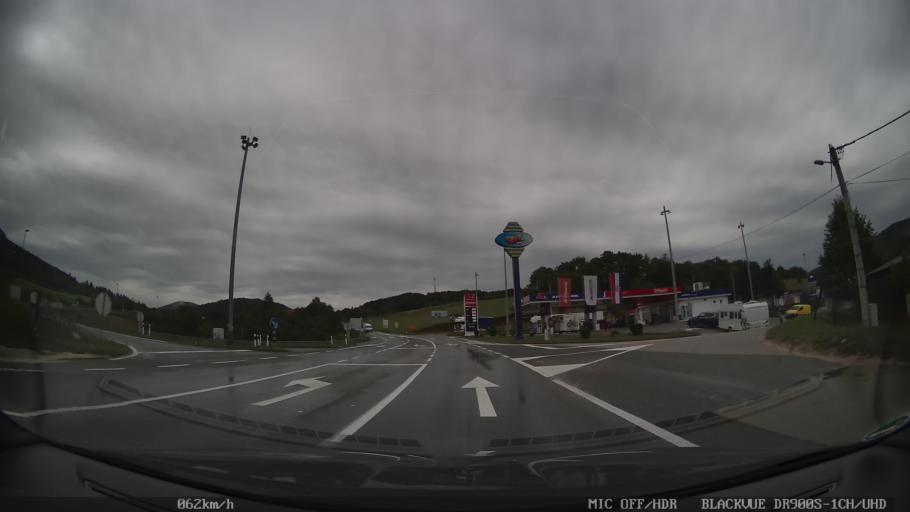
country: HR
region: Licko-Senjska
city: Otocac
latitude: 44.8943
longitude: 15.1840
